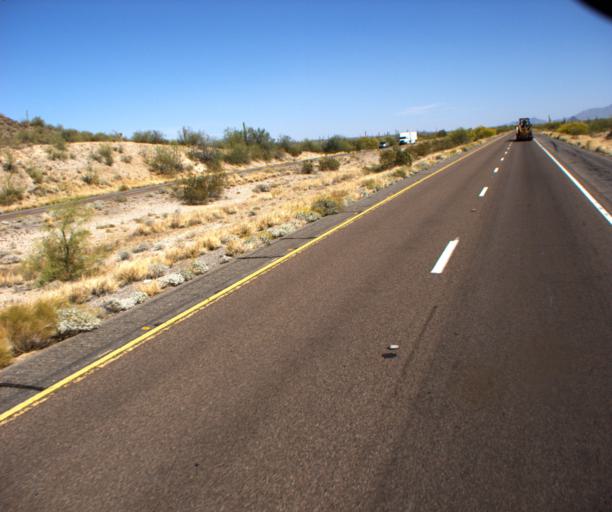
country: US
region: Arizona
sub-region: Maricopa County
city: Gila Bend
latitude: 32.8635
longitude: -112.4074
